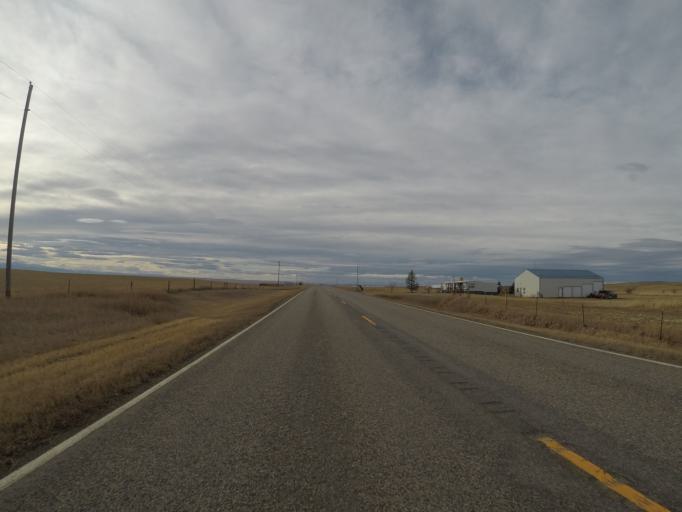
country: US
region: Montana
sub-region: Yellowstone County
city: Laurel
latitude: 45.8565
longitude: -108.8271
